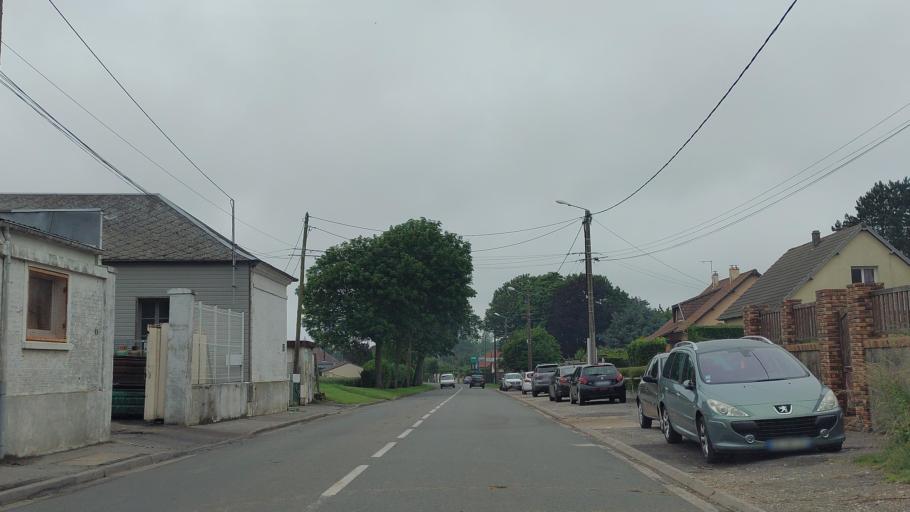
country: FR
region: Picardie
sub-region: Departement de la Somme
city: Bethencourt-sur-Mer
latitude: 50.0830
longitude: 1.4965
